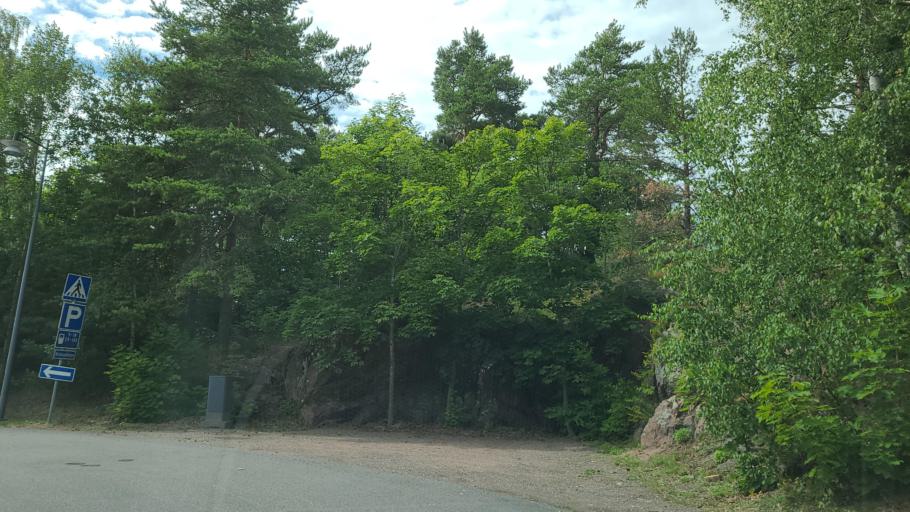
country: FI
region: Varsinais-Suomi
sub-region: Turku
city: Naantali
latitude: 60.4702
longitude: 22.0235
